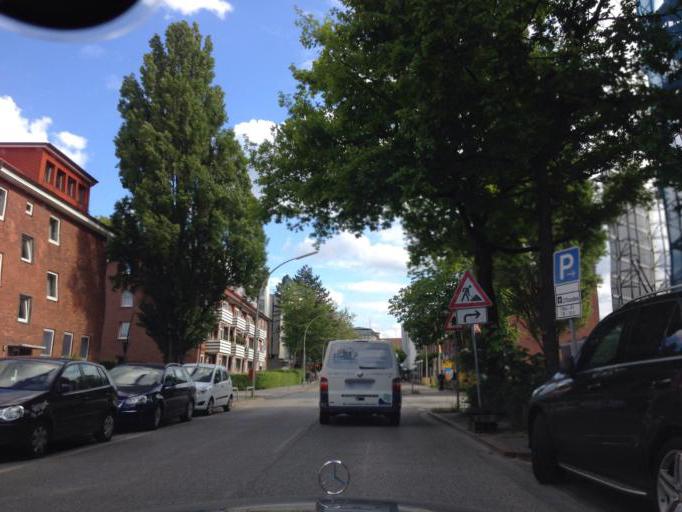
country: DE
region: Hamburg
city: Marienthal
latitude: 53.5737
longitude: 10.0633
